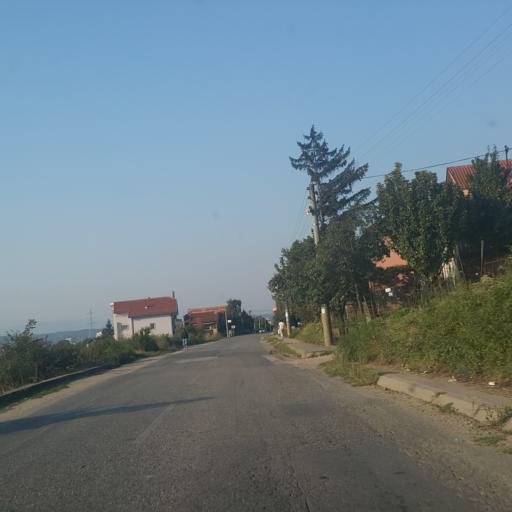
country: RS
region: Central Serbia
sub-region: Zajecarski Okrug
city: Zajecar
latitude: 43.9177
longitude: 22.2886
